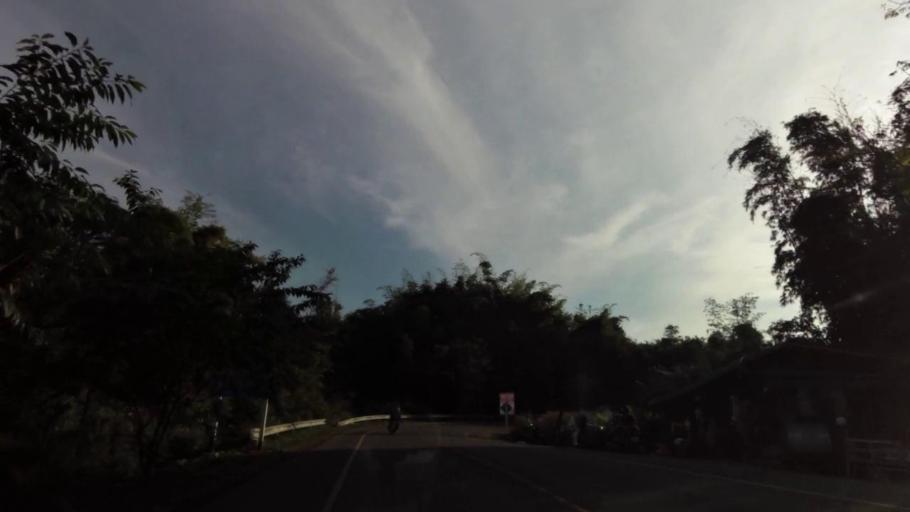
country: TH
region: Chiang Rai
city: Khun Tan
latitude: 19.8595
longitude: 100.4292
